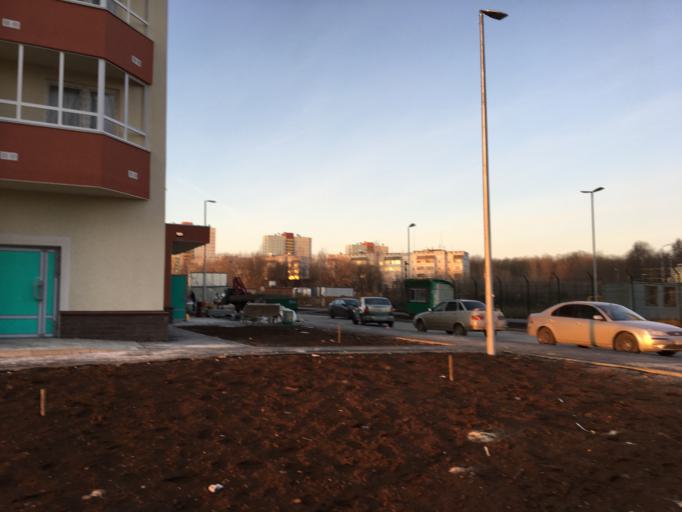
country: RU
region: Nizjnij Novgorod
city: Nizhniy Novgorod
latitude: 56.2619
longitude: 44.0129
